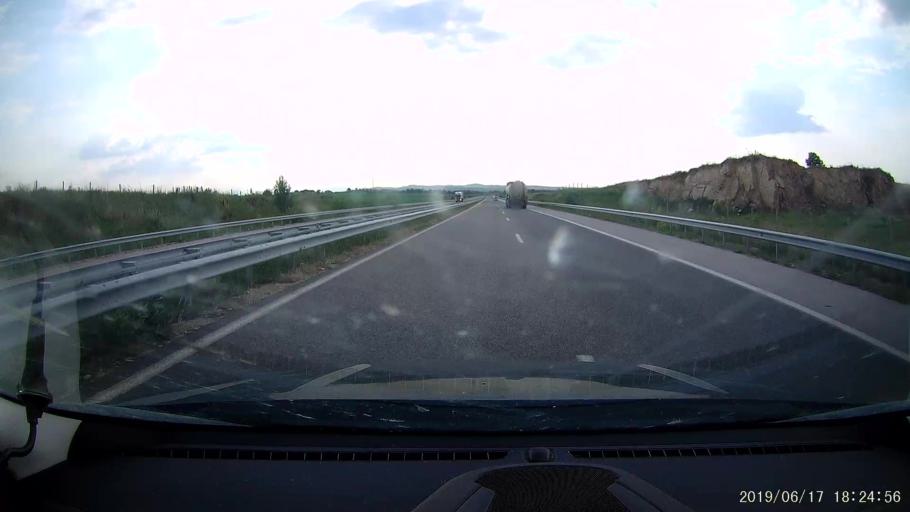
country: BG
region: Khaskovo
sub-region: Obshtina Dimitrovgrad
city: Dimitrovgrad
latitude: 41.9887
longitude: 25.6766
